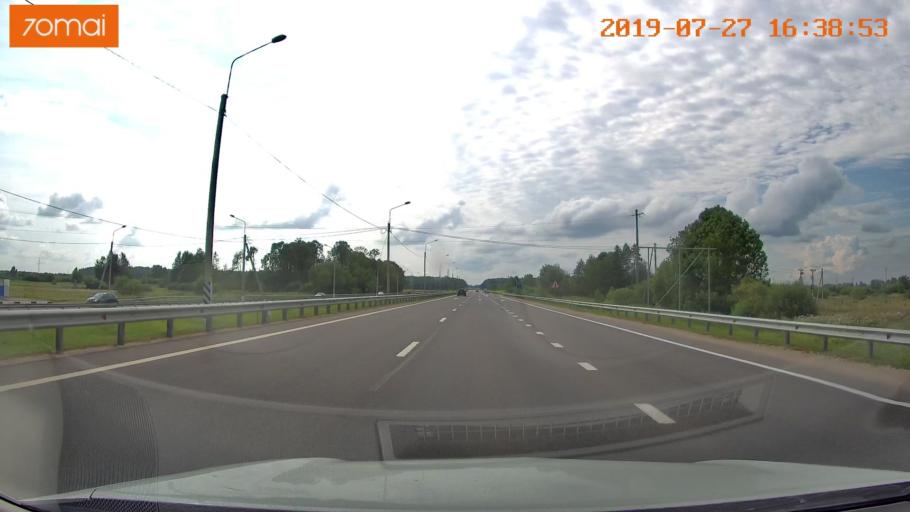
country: RU
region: Kaliningrad
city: Gvardeysk
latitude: 54.6491
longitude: 21.2160
